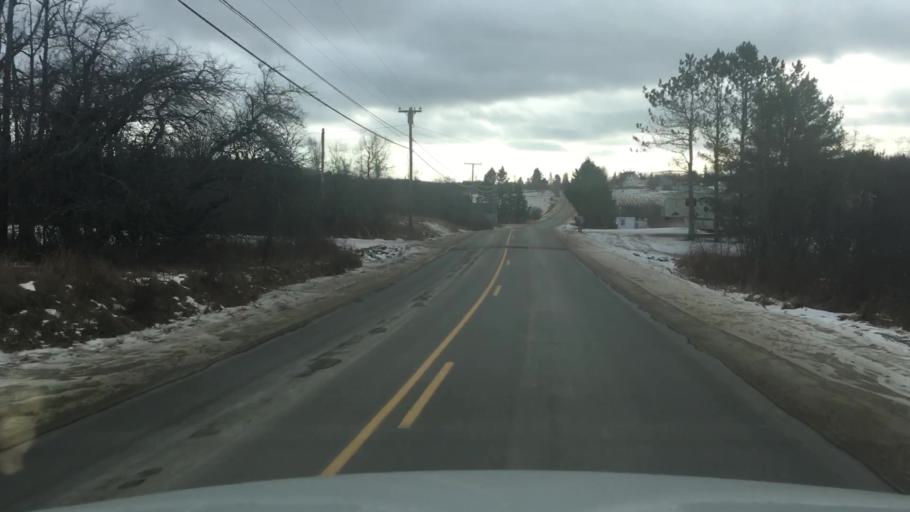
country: US
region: Maine
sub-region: Washington County
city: Machias
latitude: 44.6797
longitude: -67.4675
